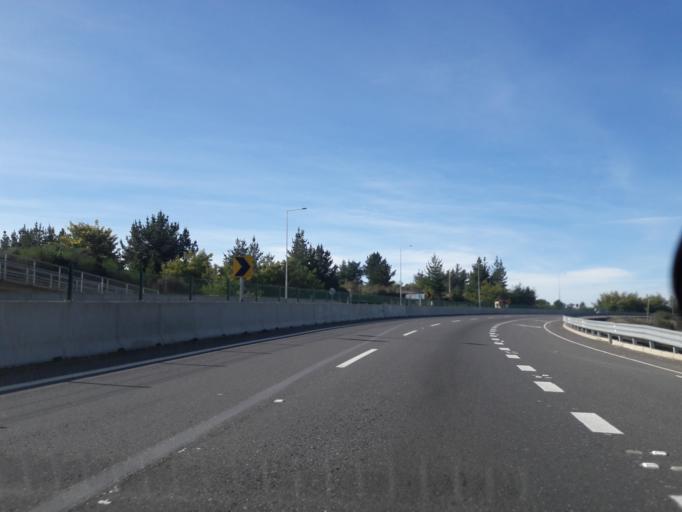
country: CL
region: Biobio
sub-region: Provincia de Biobio
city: Yumbel
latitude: -36.9740
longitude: -72.6556
